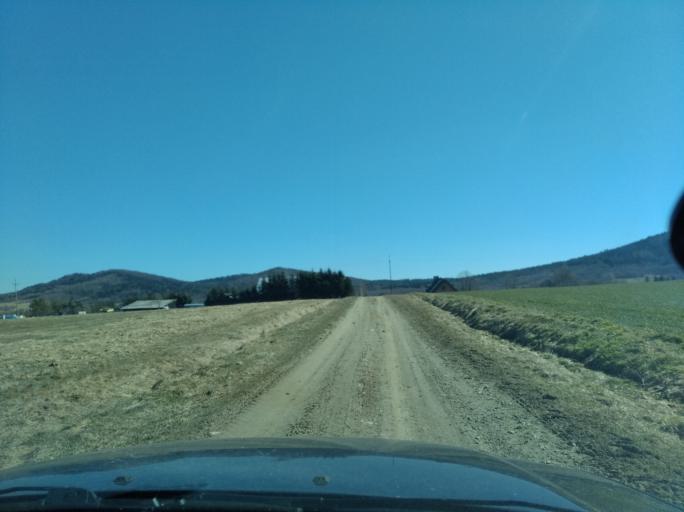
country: PL
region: Subcarpathian Voivodeship
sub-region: Powiat krosnienski
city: Korczyna
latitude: 49.7776
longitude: 21.8487
